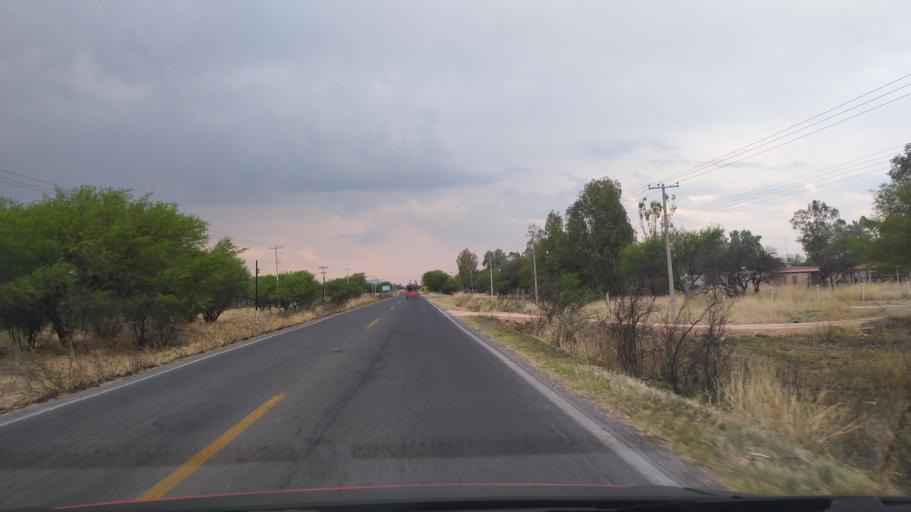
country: MX
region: Guanajuato
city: Ciudad Manuel Doblado
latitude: 20.7961
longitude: -101.9059
